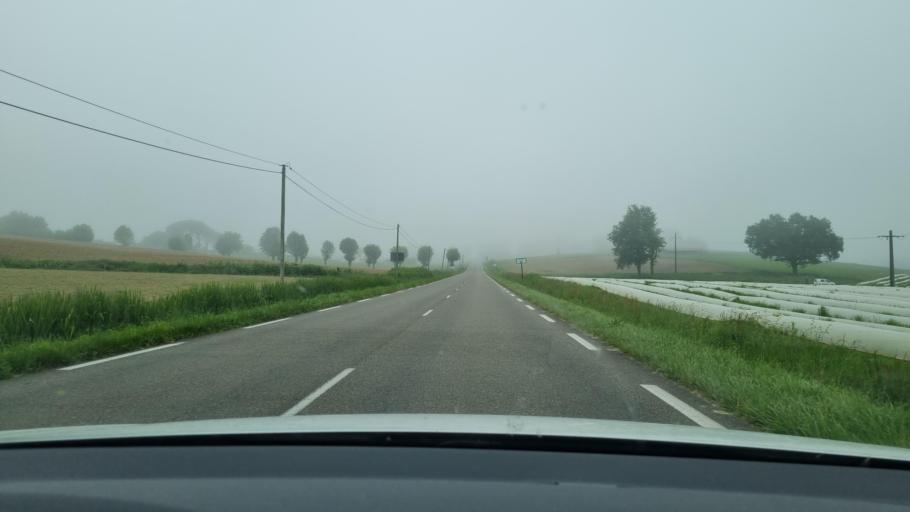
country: FR
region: Aquitaine
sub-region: Departement des Landes
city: Amou
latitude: 43.5696
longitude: -0.6610
